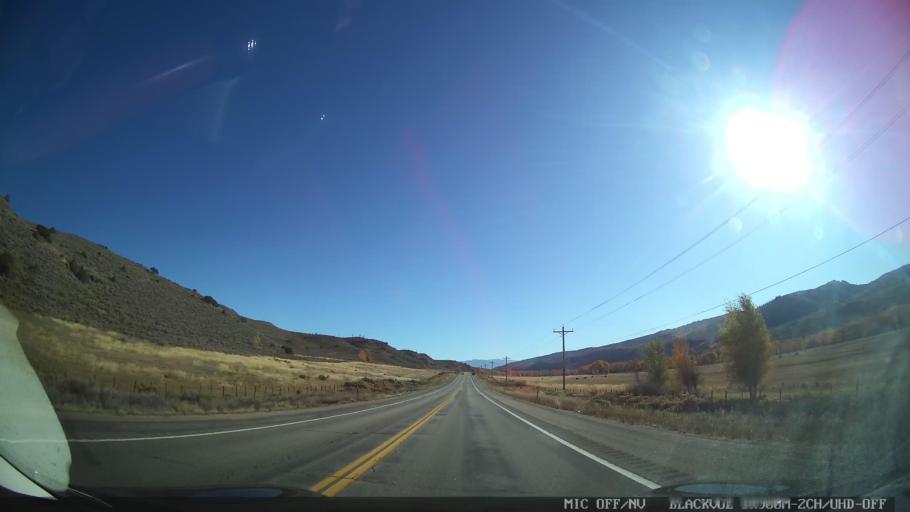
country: US
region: Colorado
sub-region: Grand County
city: Hot Sulphur Springs
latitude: 40.0952
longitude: -106.0588
